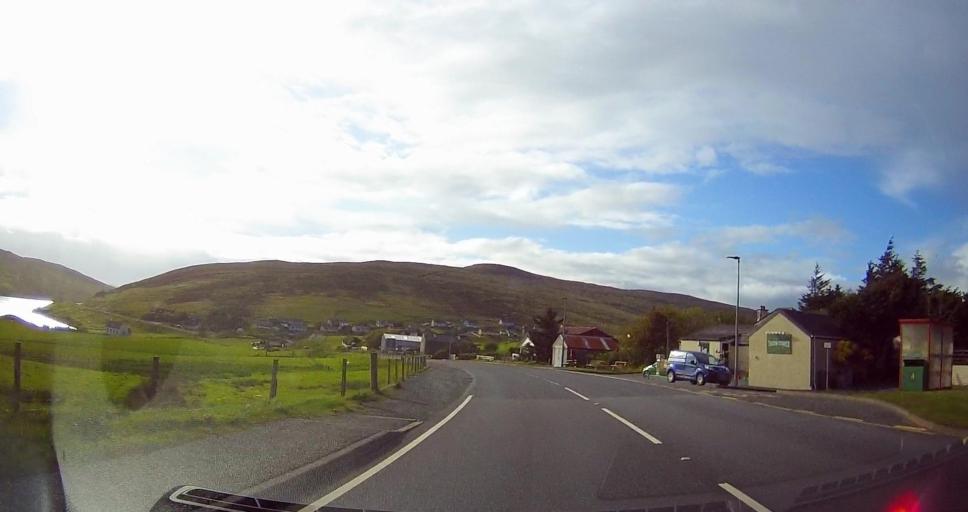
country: GB
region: Scotland
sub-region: Shetland Islands
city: Lerwick
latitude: 60.3551
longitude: -1.2620
